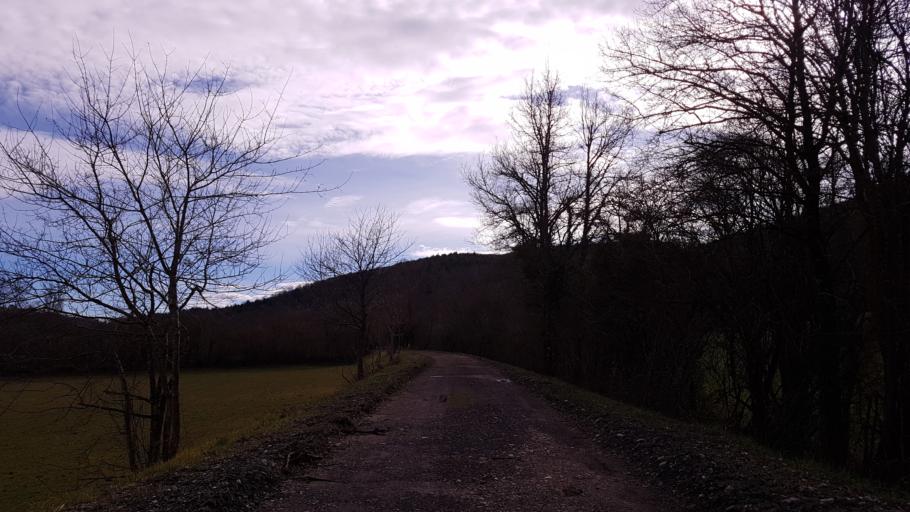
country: FR
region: Languedoc-Roussillon
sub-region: Departement de l'Aude
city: Chalabre
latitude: 43.0056
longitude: 1.9873
